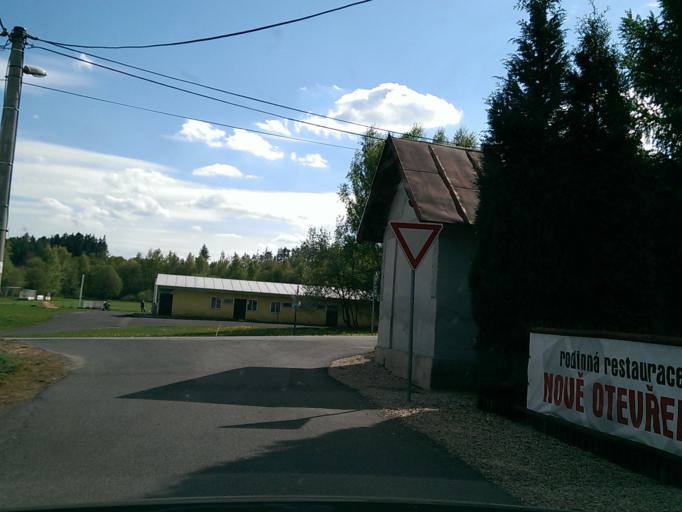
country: CZ
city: Pencin
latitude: 50.6878
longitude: 15.2360
